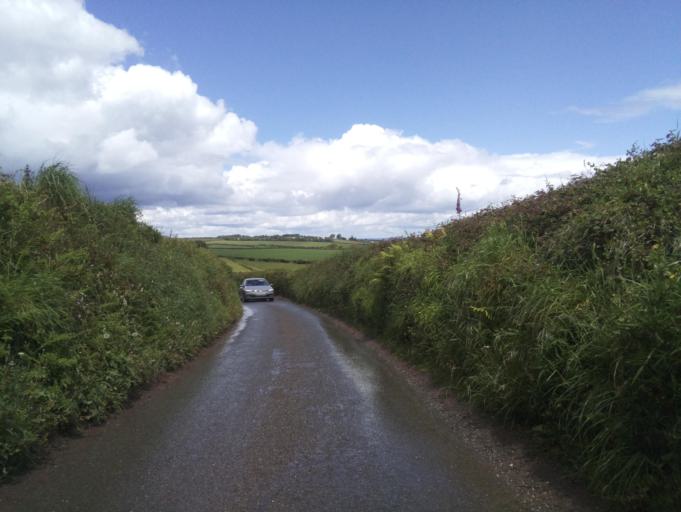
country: GB
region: England
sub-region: Devon
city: Dartmouth
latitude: 50.3519
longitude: -3.5375
